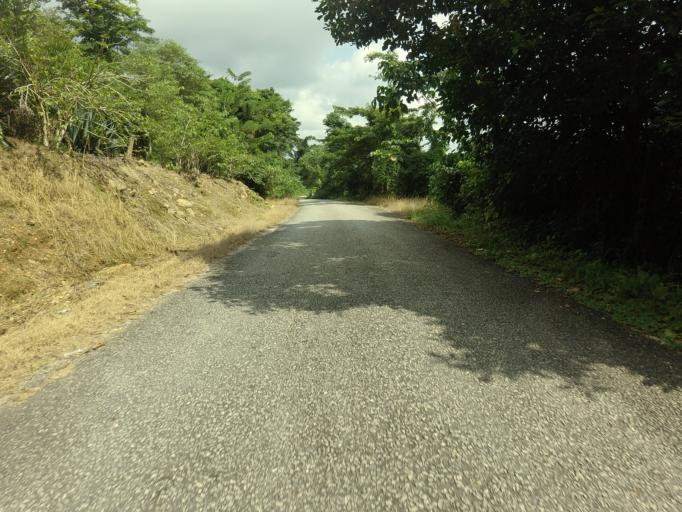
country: GH
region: Volta
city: Kpandu
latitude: 6.8282
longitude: 0.4250
